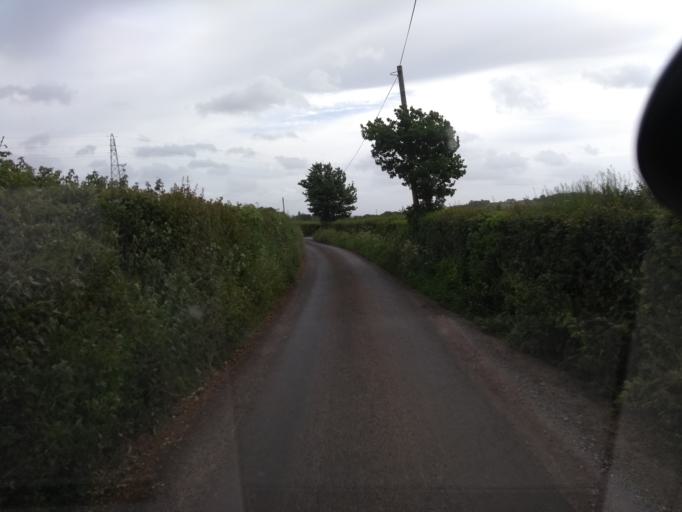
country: GB
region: England
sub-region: Somerset
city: North Petherton
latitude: 51.1360
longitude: -3.1096
